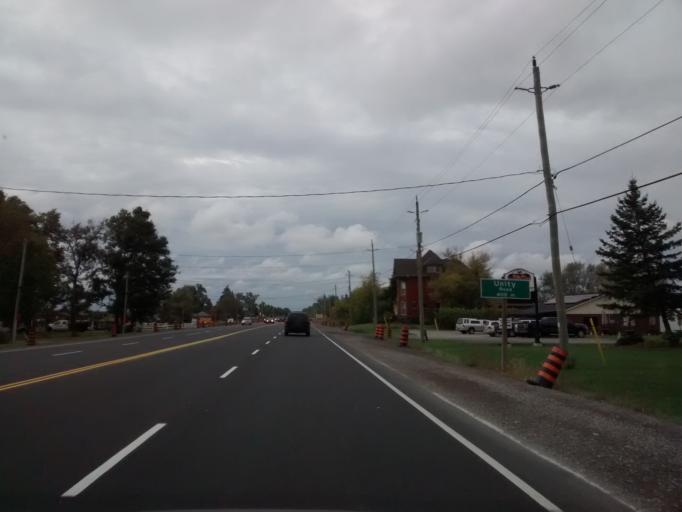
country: CA
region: Ontario
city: Ancaster
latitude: 43.1106
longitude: -79.9352
